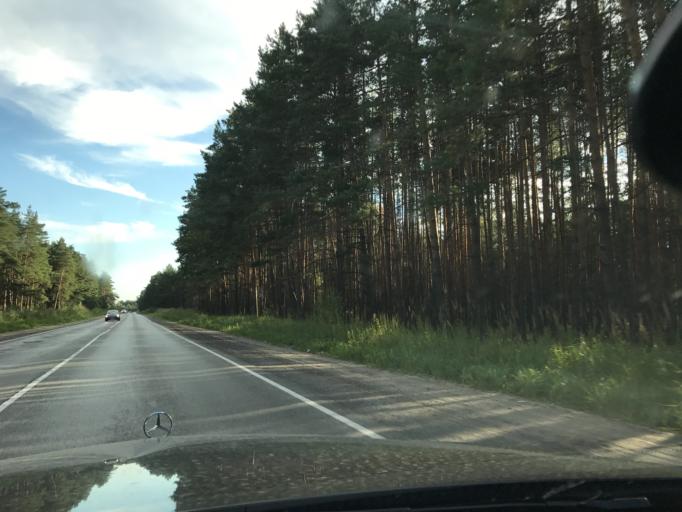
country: RU
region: Vladimir
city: Kommunar
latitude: 56.0457
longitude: 40.4349
